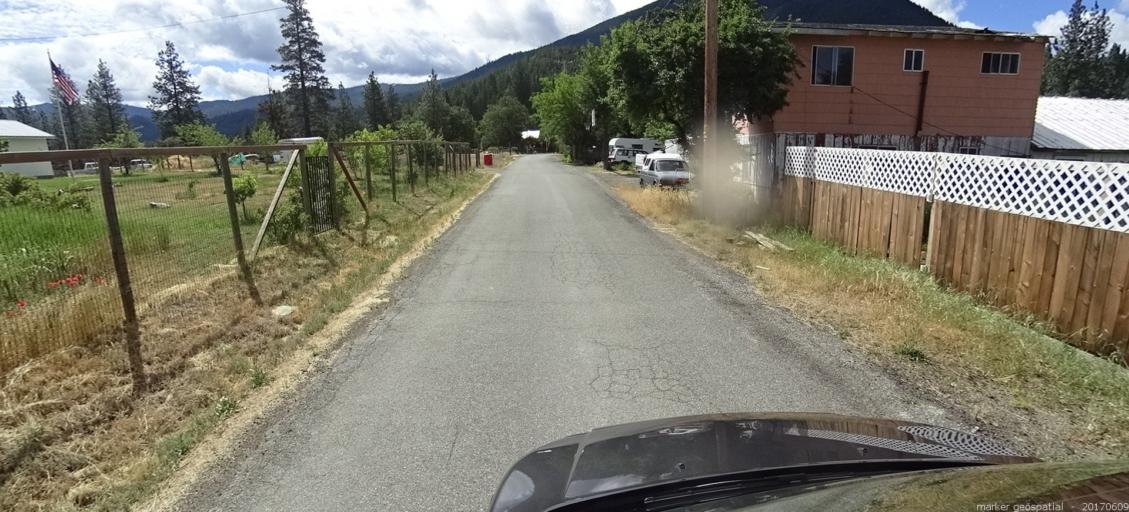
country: US
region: California
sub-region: Siskiyou County
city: Weed
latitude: 41.3076
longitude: -122.8001
